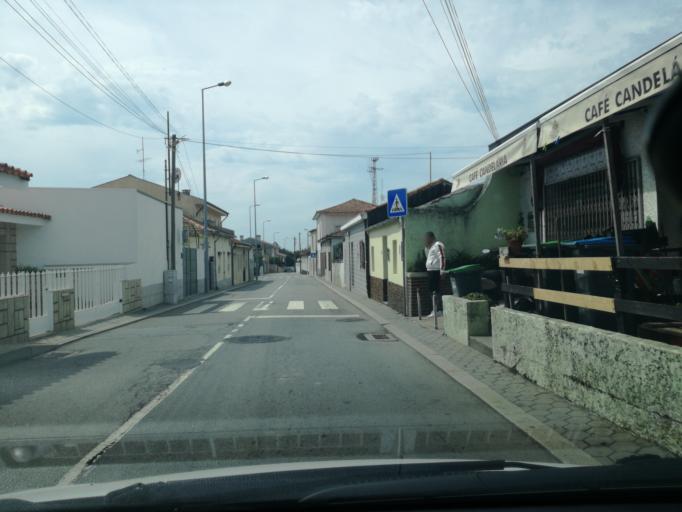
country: PT
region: Porto
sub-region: Vila Nova de Gaia
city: Grijo
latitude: 41.0422
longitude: -8.5764
